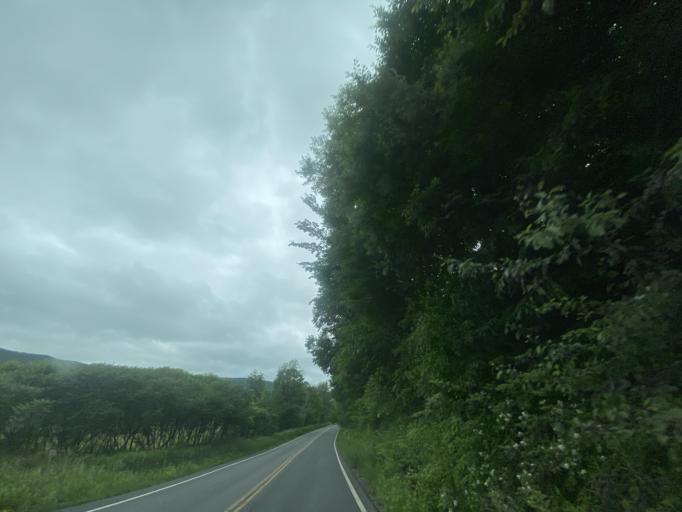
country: US
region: New York
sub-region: Schoharie County
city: Middleburgh
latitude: 42.3884
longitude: -74.3447
